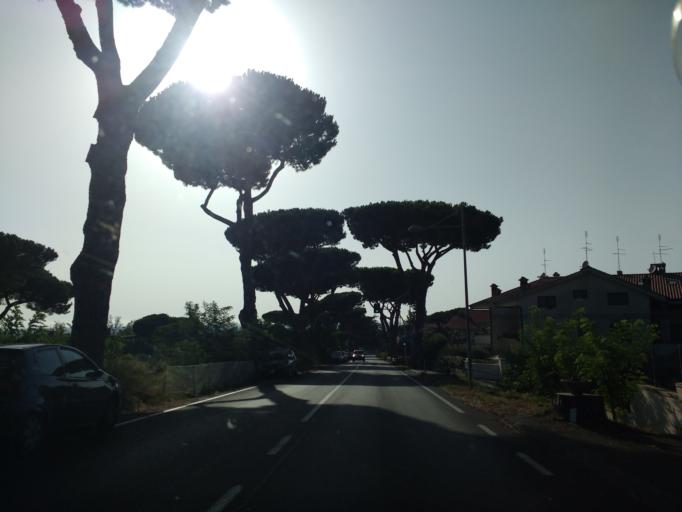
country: IT
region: Latium
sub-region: Citta metropolitana di Roma Capitale
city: Marino
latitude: 41.7547
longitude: 12.6322
